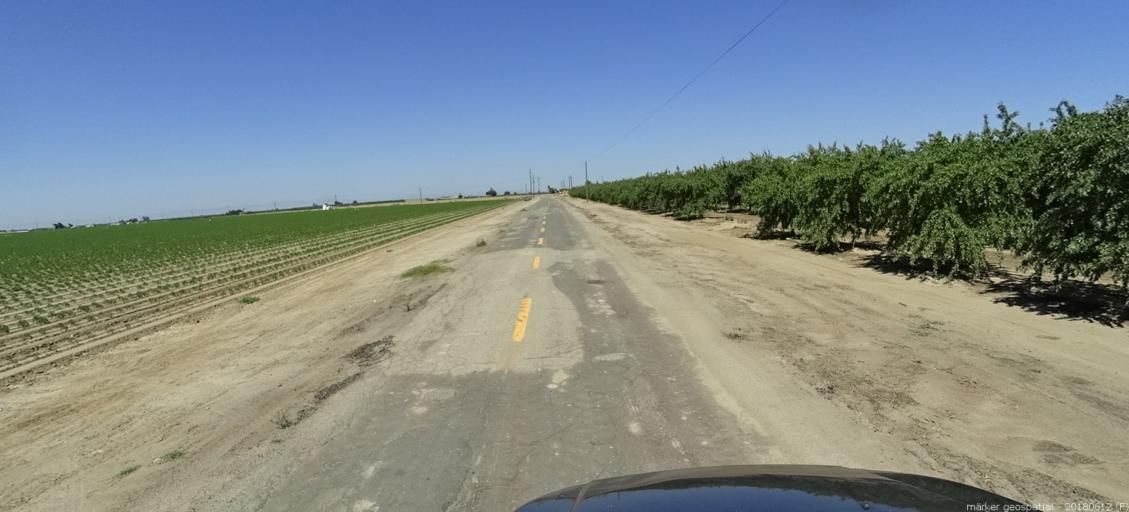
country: US
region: California
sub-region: Madera County
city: Chowchilla
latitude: 37.0254
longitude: -120.3378
